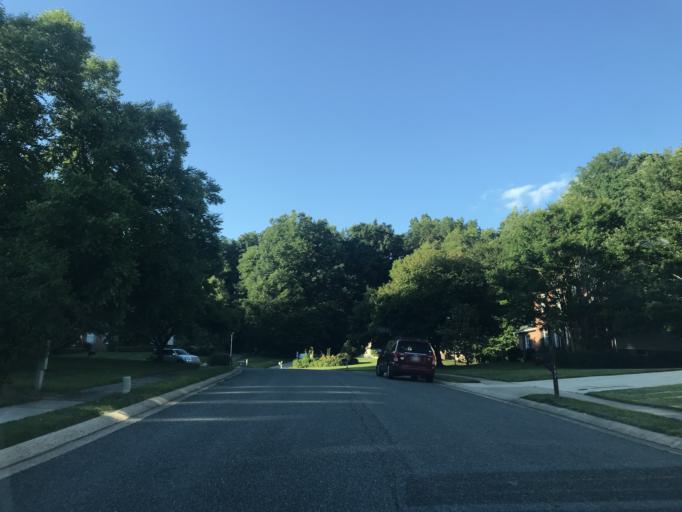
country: US
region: Maryland
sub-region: Harford County
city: South Bel Air
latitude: 39.5601
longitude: -76.3180
